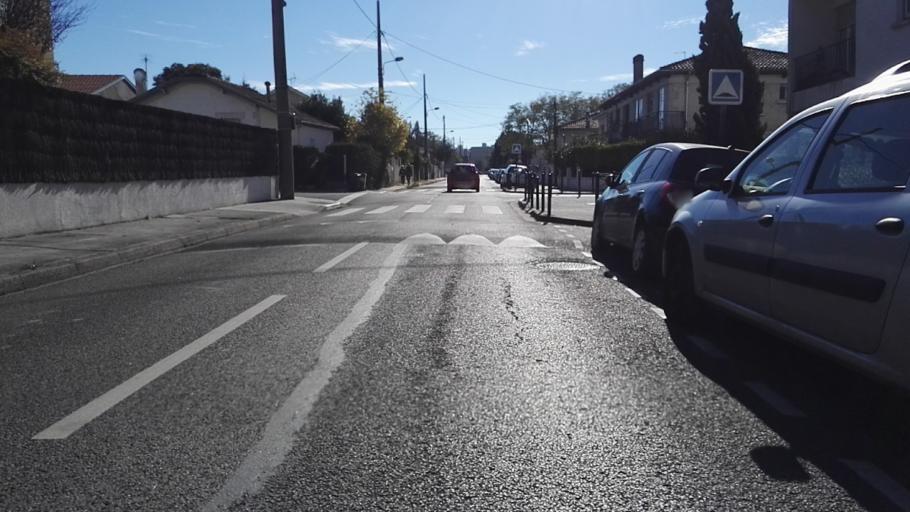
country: FR
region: Aquitaine
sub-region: Departement de la Gironde
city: Bruges
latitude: 44.8615
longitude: -0.6191
